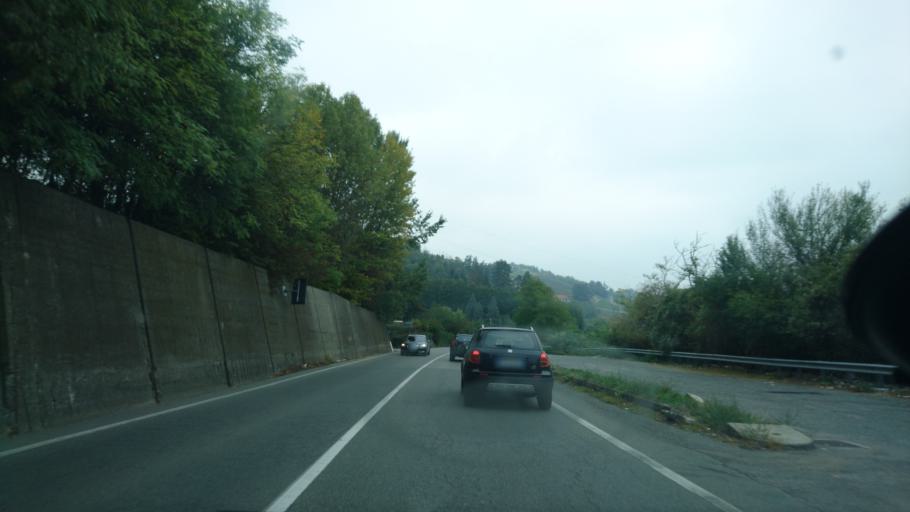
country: IT
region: Piedmont
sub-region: Provincia di Alessandria
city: Terzo
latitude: 44.6741
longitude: 8.4297
